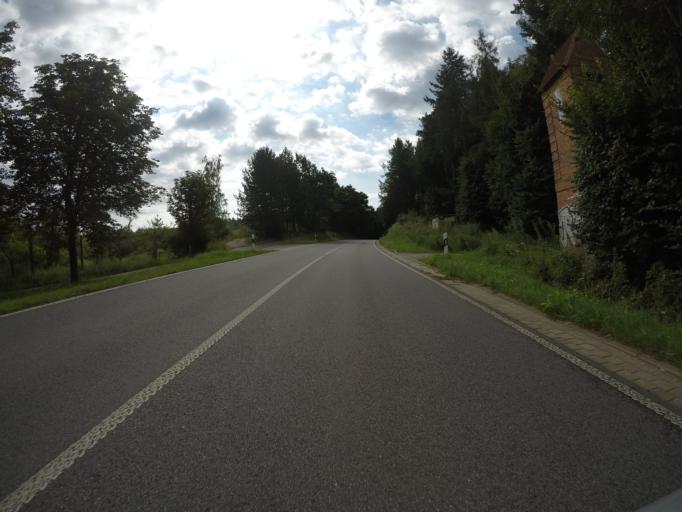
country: DE
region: Brandenburg
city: Rheinsberg
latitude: 53.1740
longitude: 12.8875
